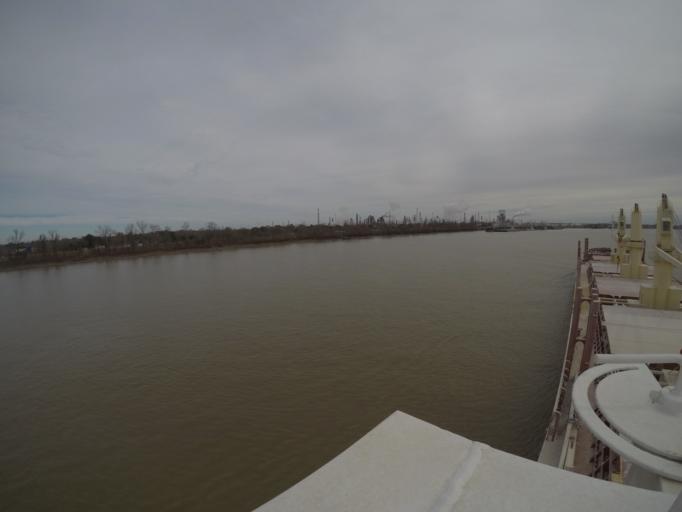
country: US
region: Louisiana
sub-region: Saint Charles Parish
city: Norco
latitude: 29.9944
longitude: -90.4200
